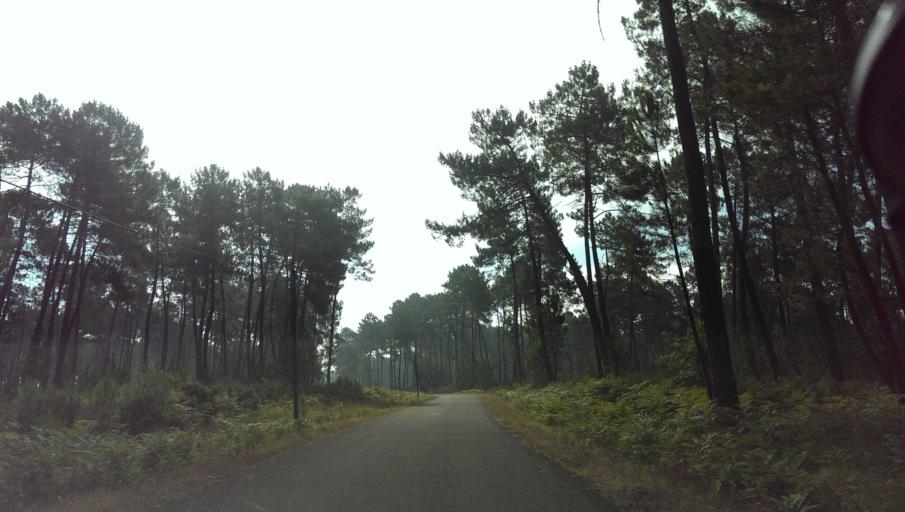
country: FR
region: Aquitaine
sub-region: Departement des Landes
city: Gabarret
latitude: 44.1122
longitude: -0.0697
